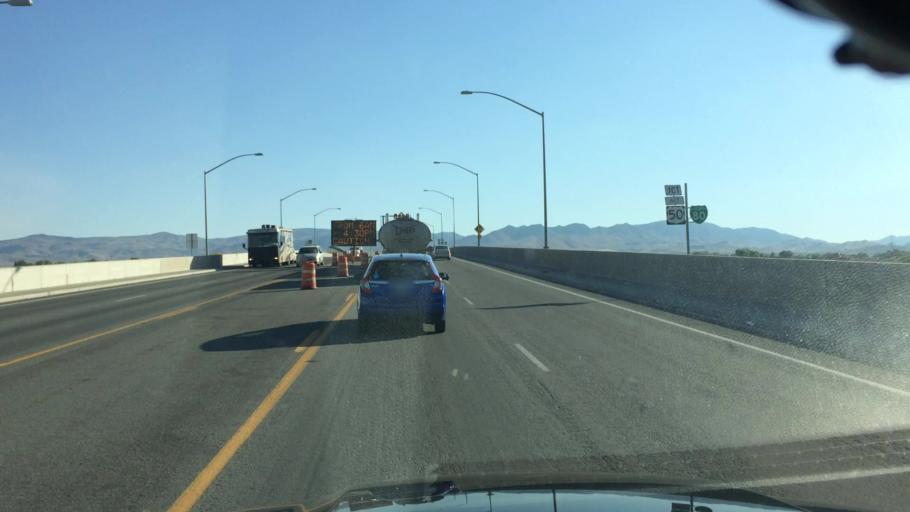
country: US
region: Nevada
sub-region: Lyon County
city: Fernley
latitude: 39.6064
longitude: -119.2242
